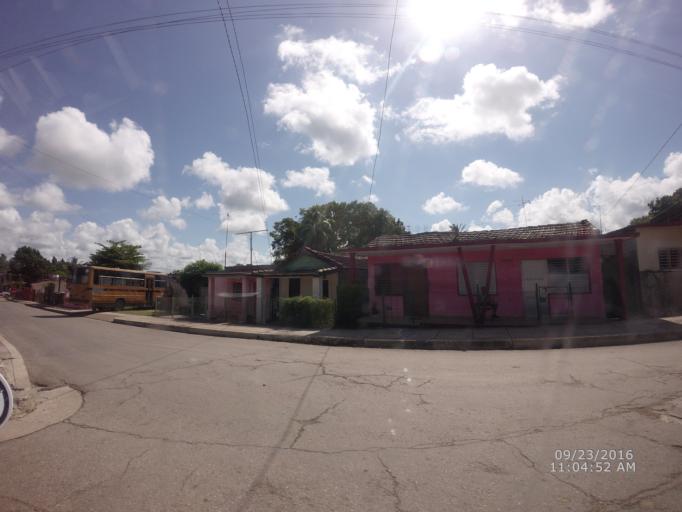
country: CU
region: Mayabeque
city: Jamaica
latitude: 23.0041
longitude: -82.2167
